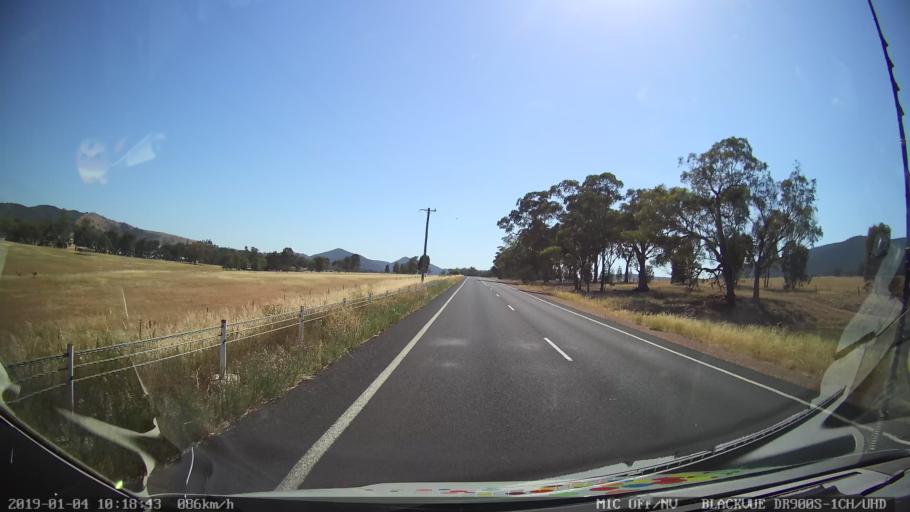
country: AU
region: New South Wales
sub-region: Cabonne
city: Canowindra
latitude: -33.3806
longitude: 148.4705
